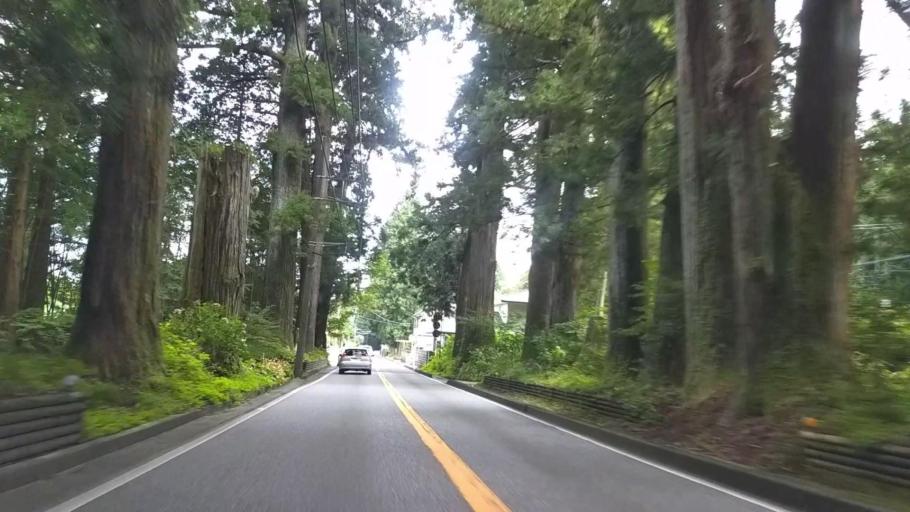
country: JP
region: Tochigi
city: Nikko
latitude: 36.7382
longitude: 139.6394
